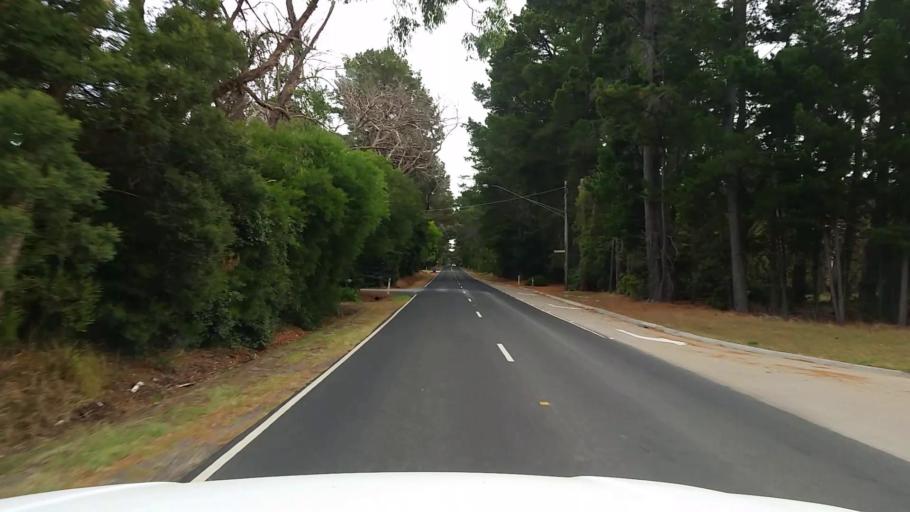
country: AU
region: Victoria
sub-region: Mornington Peninsula
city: Balnarring
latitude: -38.3704
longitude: 145.1236
